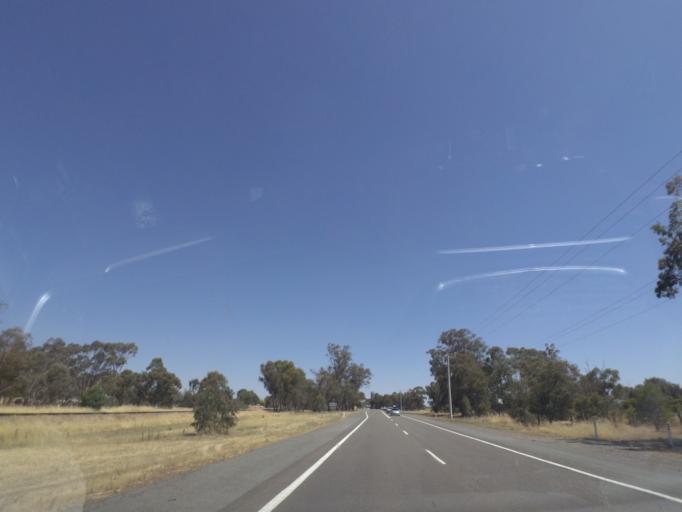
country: AU
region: Victoria
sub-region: Greater Shepparton
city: Shepparton
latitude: -36.2345
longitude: 145.4318
